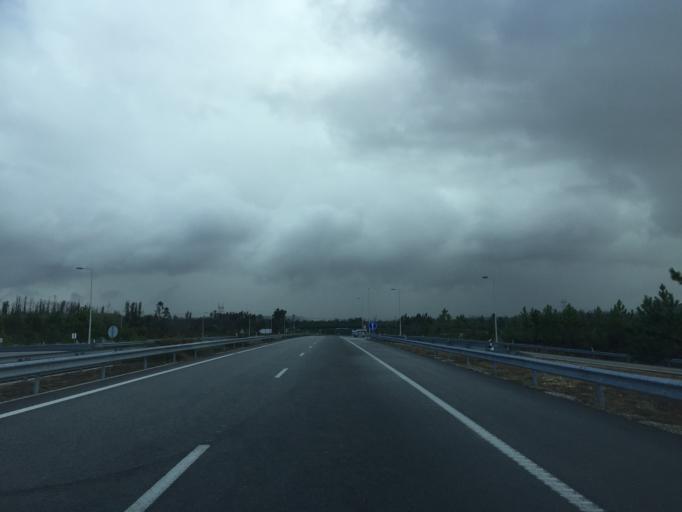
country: PT
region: Coimbra
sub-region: Cantanhede
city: Cantanhede
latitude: 40.2852
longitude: -8.5254
